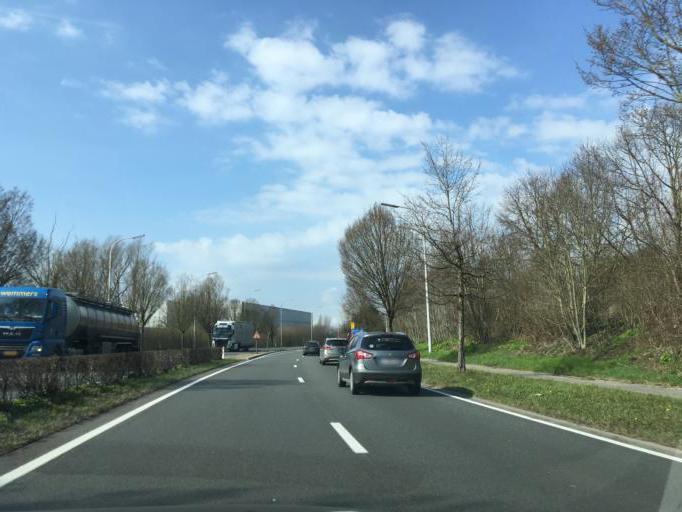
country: BE
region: Flanders
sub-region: Provincie West-Vlaanderen
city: Deerlijk
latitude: 50.8455
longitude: 3.3554
